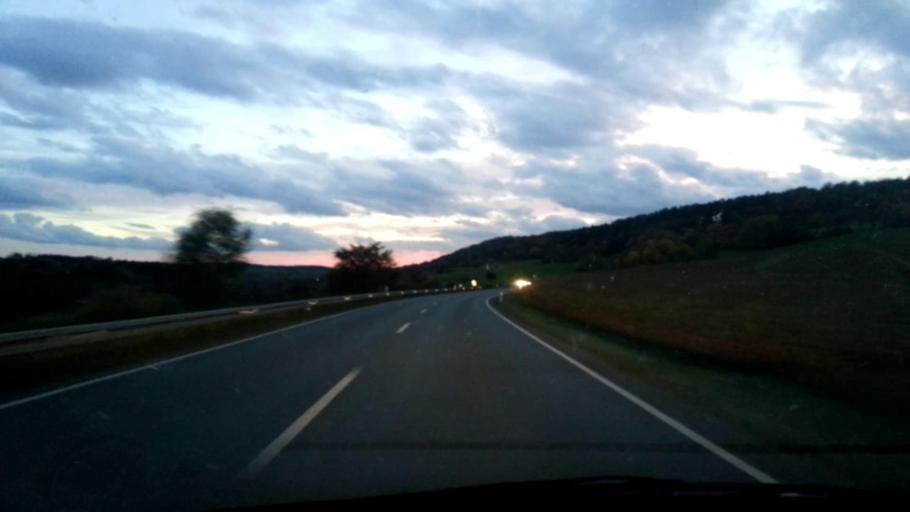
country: DE
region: Bavaria
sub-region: Upper Franconia
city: Reuth
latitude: 49.9727
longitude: 11.6715
